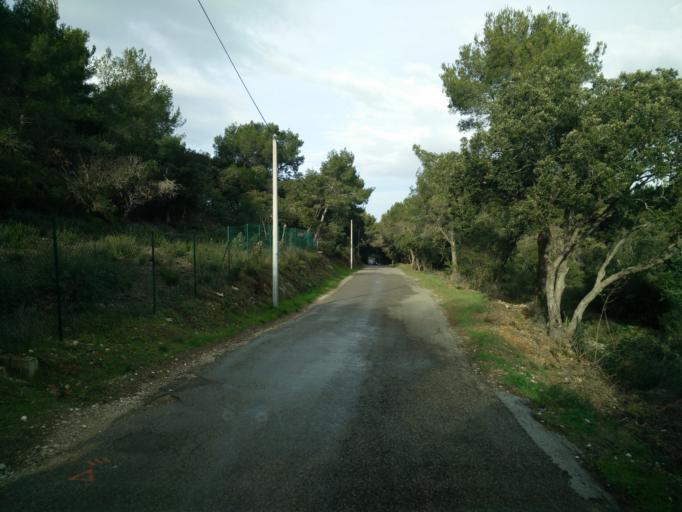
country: FR
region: Provence-Alpes-Cote d'Azur
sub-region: Departement du Var
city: Six-Fours-les-Plages
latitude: 43.0678
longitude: 5.8263
